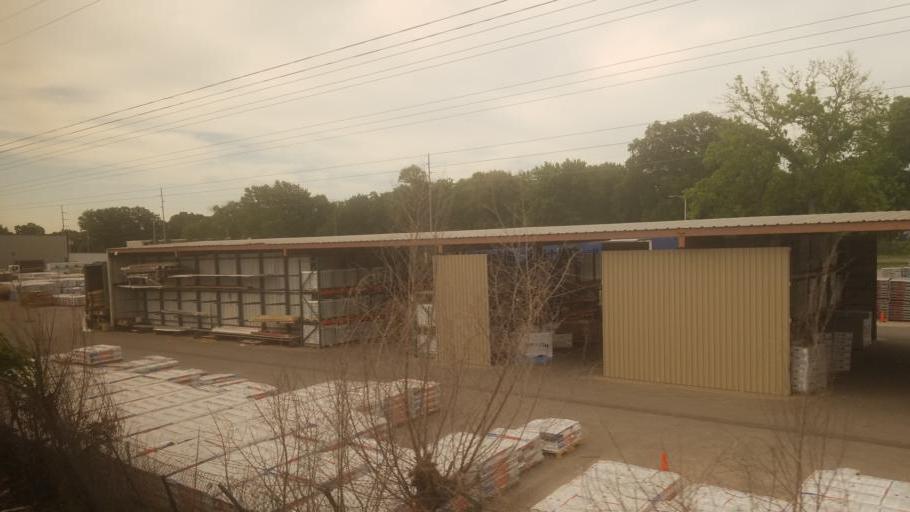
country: US
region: Kansas
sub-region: Shawnee County
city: Topeka
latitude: 39.0544
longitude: -95.6568
